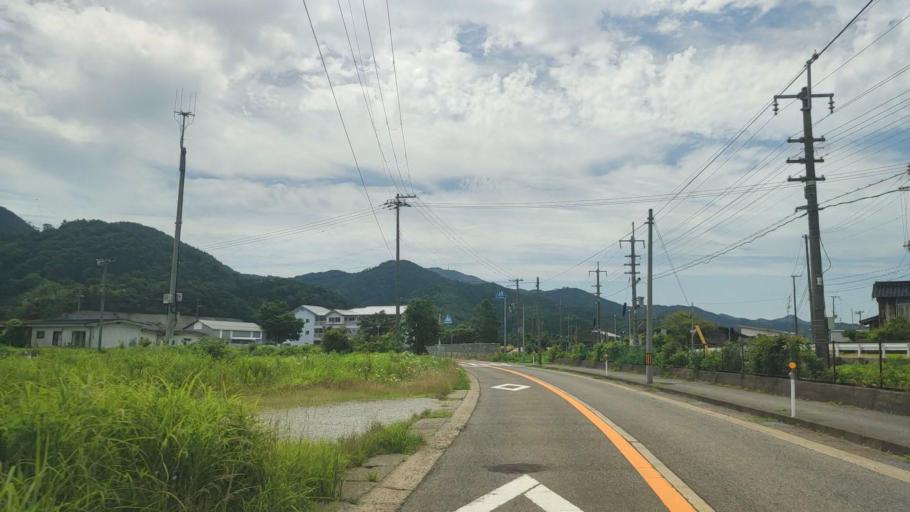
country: JP
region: Hyogo
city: Toyooka
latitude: 35.6481
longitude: 134.7578
